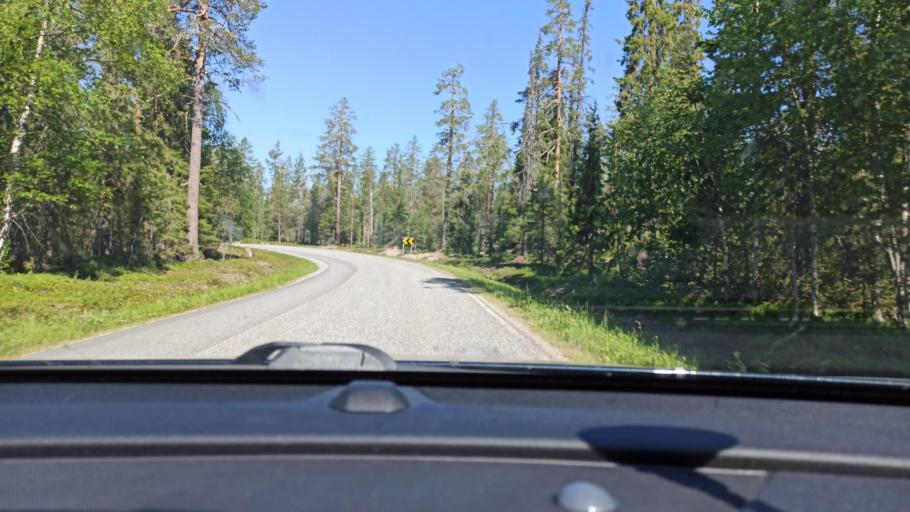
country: FI
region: Lapland
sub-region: Tunturi-Lappi
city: Kolari
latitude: 67.6682
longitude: 24.1590
